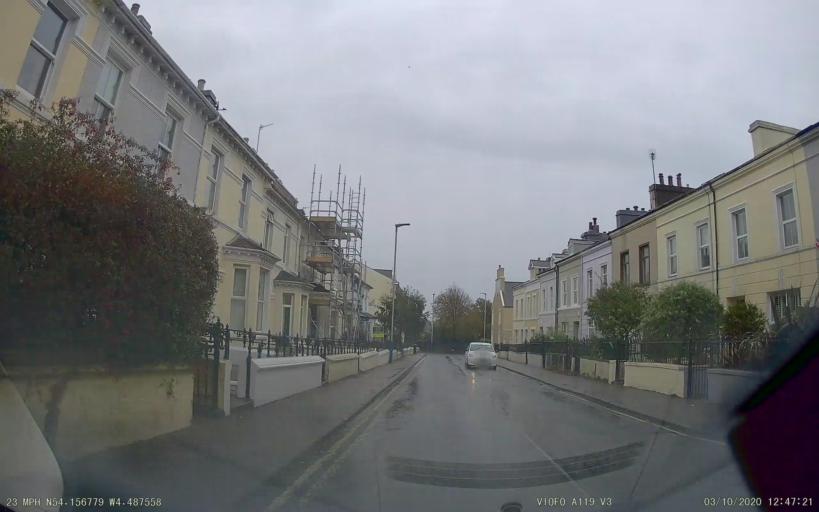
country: IM
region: Douglas
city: Douglas
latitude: 54.1569
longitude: -4.4873
